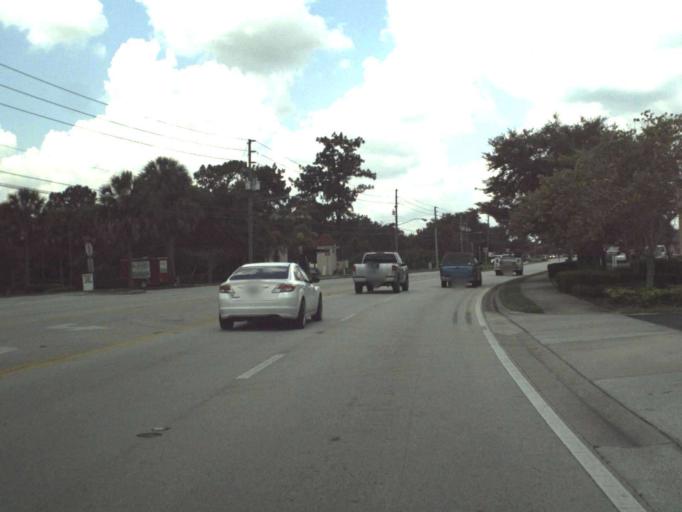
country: US
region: Florida
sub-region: Seminole County
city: Winter Springs
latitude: 28.6992
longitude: -81.3015
